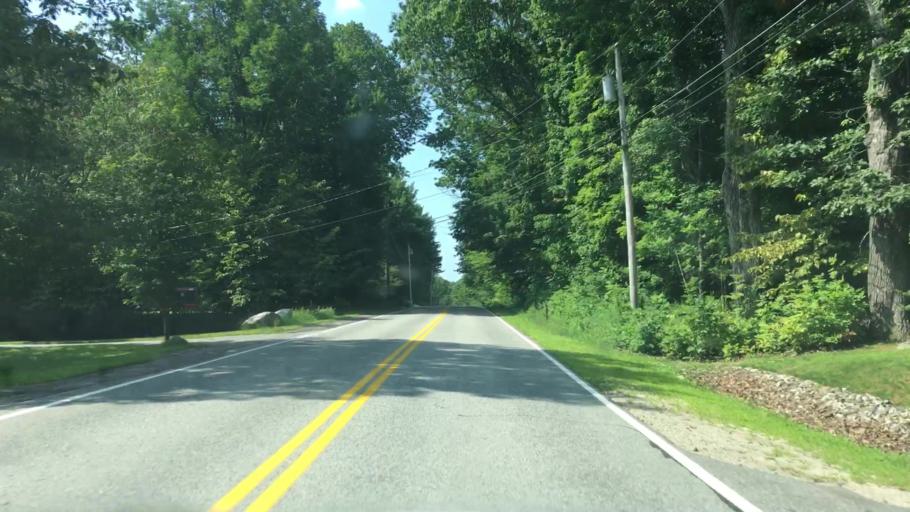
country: US
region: Maine
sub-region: Androscoggin County
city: Poland
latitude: 43.9767
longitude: -70.4051
